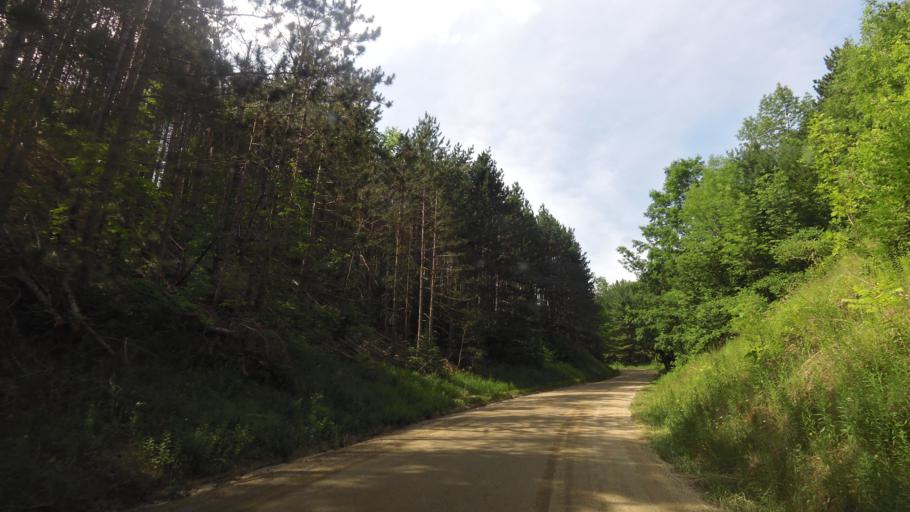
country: CA
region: Ontario
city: Orangeville
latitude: 43.9942
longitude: -80.0484
